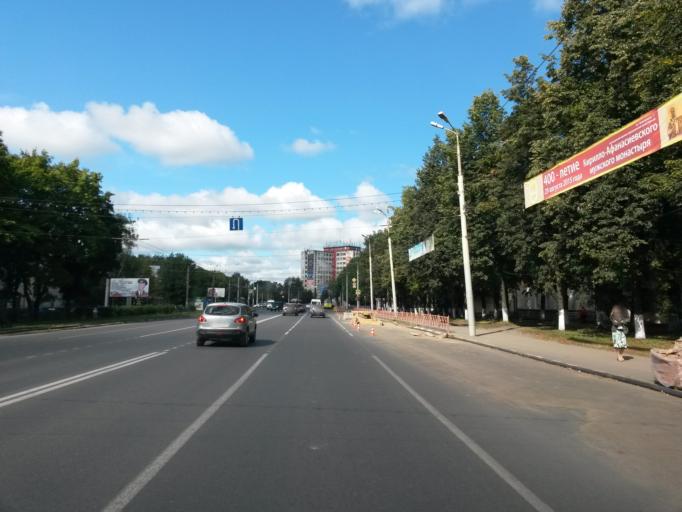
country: RU
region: Jaroslavl
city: Yaroslavl
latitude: 57.6365
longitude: 39.8633
